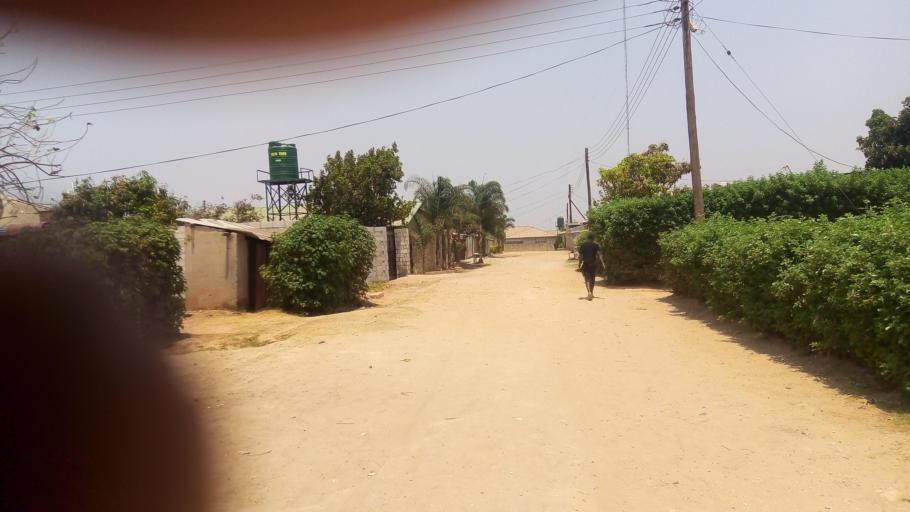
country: ZM
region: Lusaka
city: Lusaka
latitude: -15.4397
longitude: 28.3762
